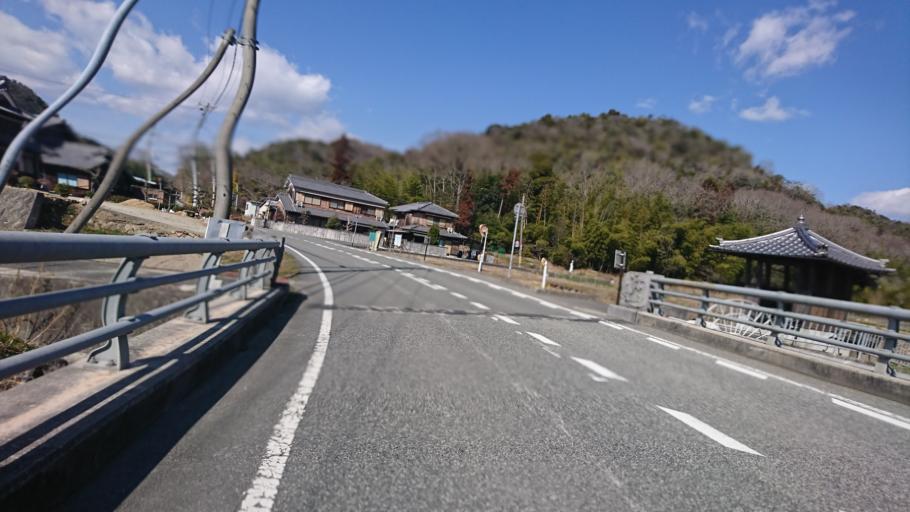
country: JP
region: Hyogo
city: Kakogawacho-honmachi
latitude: 34.8537
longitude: 134.8097
